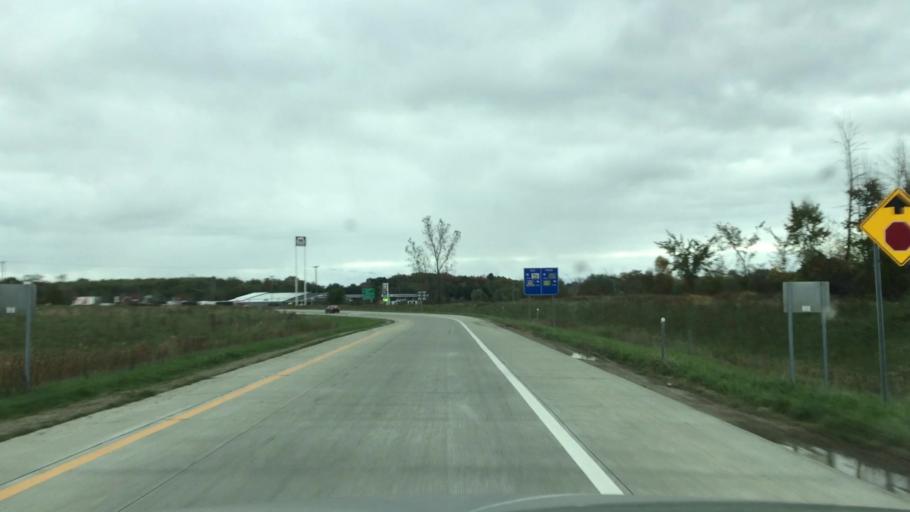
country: US
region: Michigan
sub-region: Macomb County
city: Memphis
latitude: 42.9784
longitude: -82.7680
